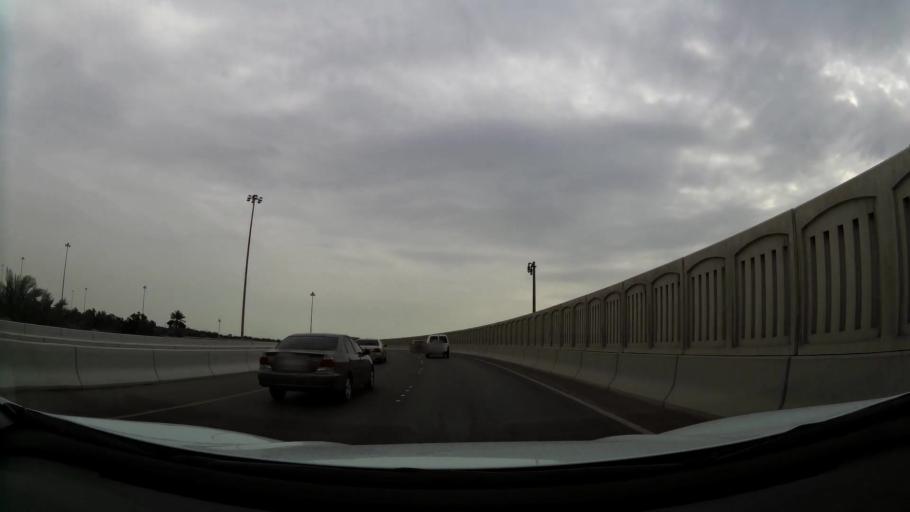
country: AE
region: Abu Dhabi
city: Abu Dhabi
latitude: 24.4224
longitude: 54.4173
